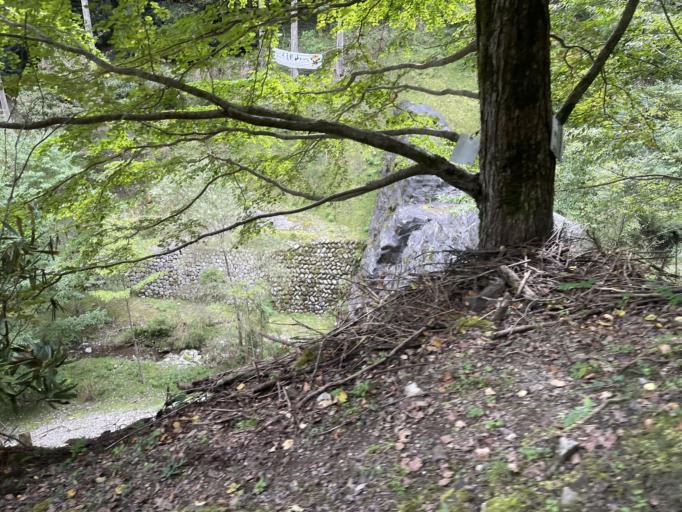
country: JP
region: Wakayama
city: Koya
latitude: 34.2319
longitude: 135.5806
